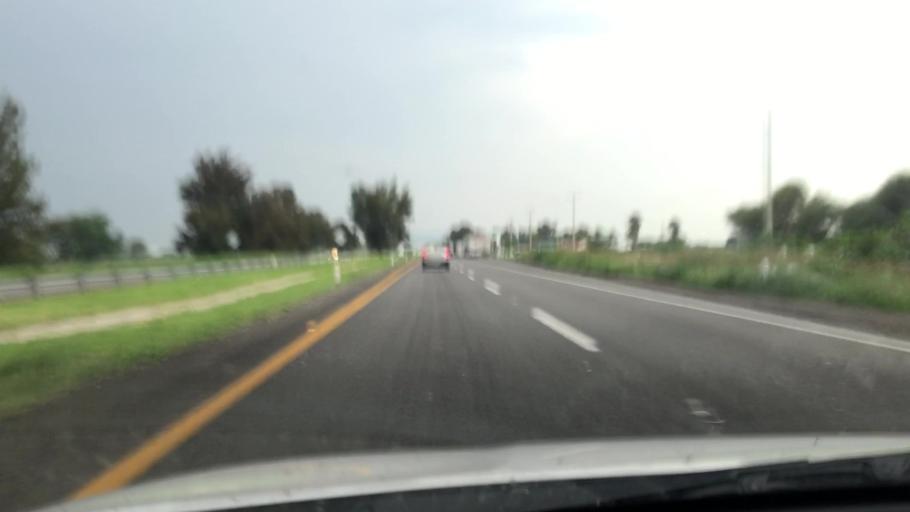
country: MX
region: Jalisco
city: La Barca
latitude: 20.3220
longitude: -102.5087
